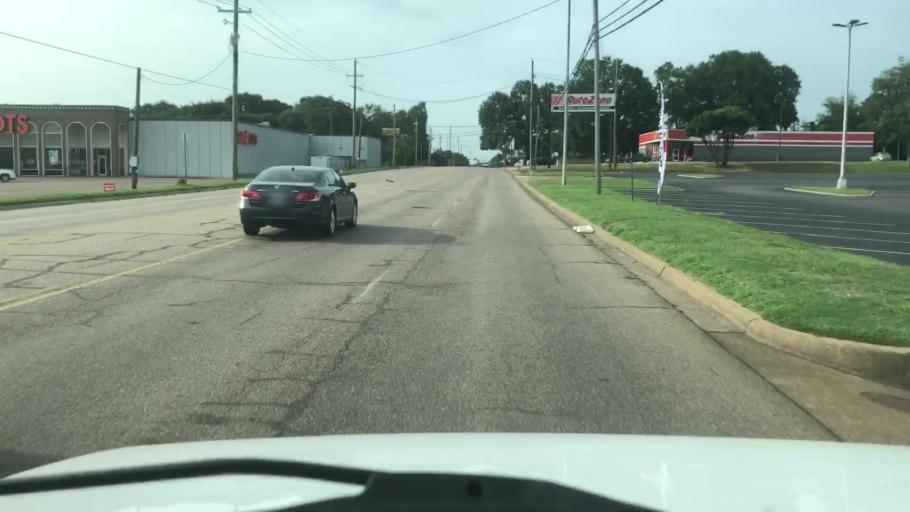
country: US
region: Texas
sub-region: Bowie County
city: Wake Village
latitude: 33.4346
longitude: -94.0805
